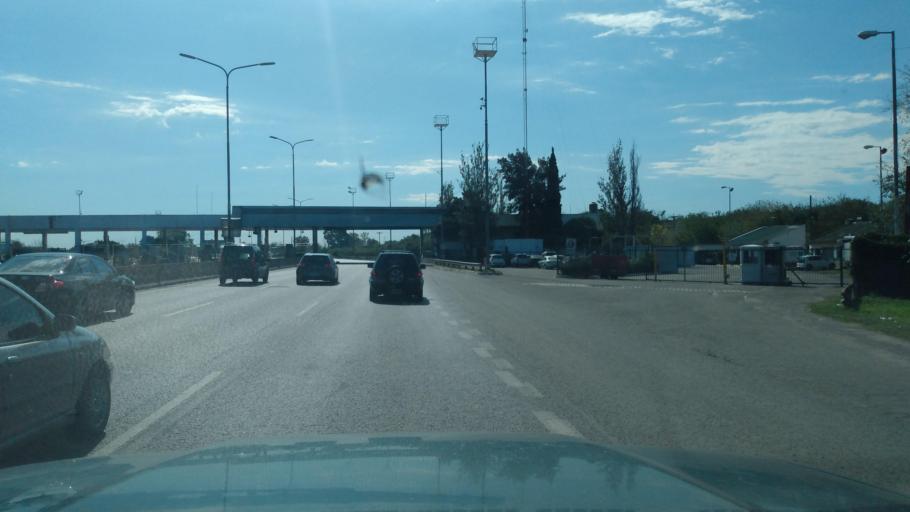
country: AR
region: Buenos Aires
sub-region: Partido de Tigre
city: Tigre
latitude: -34.5045
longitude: -58.5895
